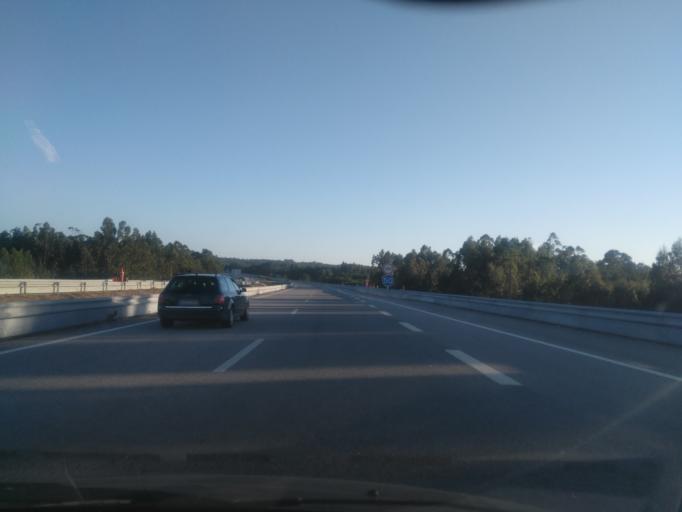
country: PT
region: Coimbra
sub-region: Figueira da Foz
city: Alhadas
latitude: 40.2098
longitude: -8.8128
